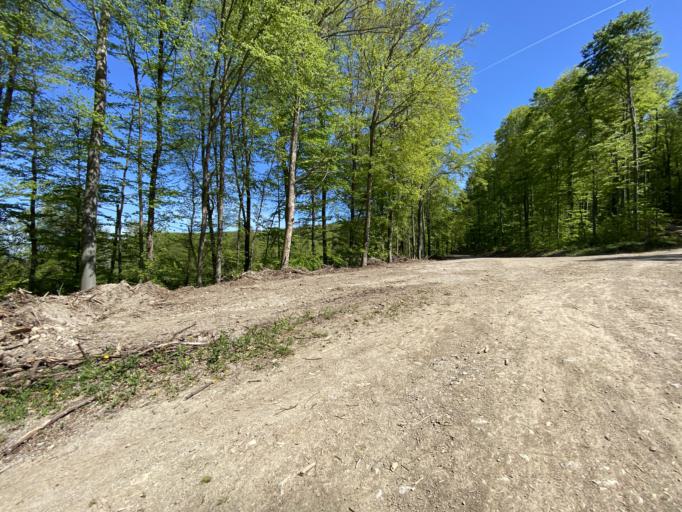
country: AT
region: Lower Austria
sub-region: Politischer Bezirk Modling
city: Breitenfurt bei Wien
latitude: 48.1005
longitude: 16.1535
